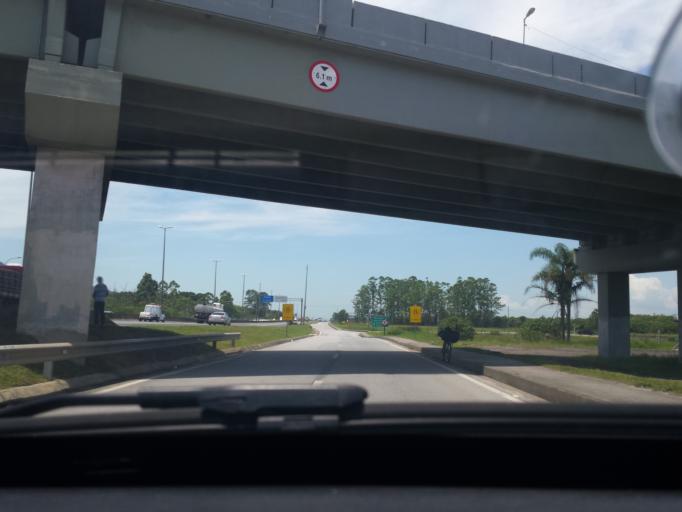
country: BR
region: Santa Catarina
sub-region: Porto Belo
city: Porto Belo
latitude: -27.1628
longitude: -48.6114
